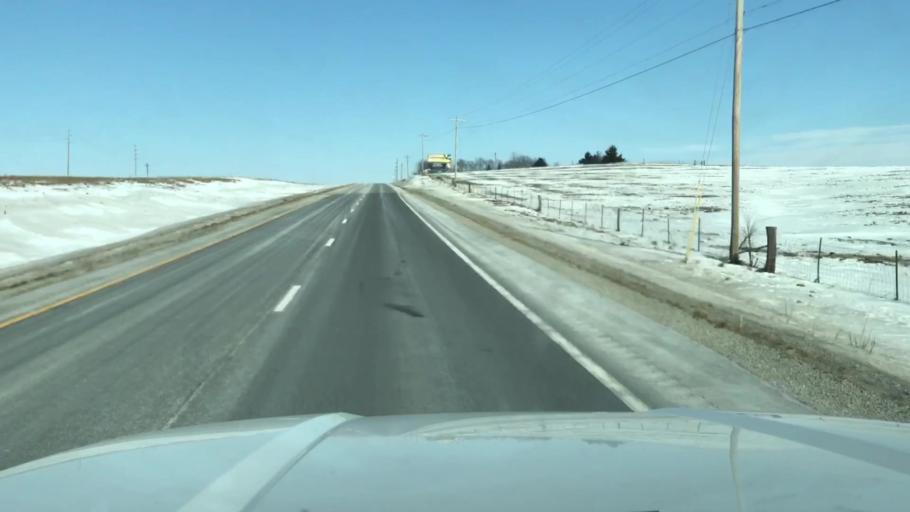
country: US
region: Missouri
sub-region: Andrew County
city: Savannah
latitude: 40.1086
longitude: -94.8698
